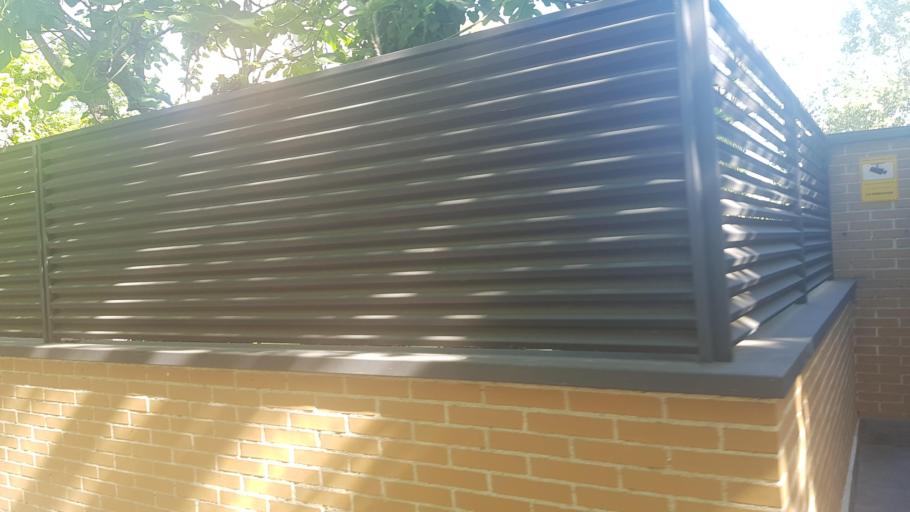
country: ES
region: Madrid
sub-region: Provincia de Madrid
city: Pozuelo de Alarcon
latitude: 40.4675
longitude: -3.7897
